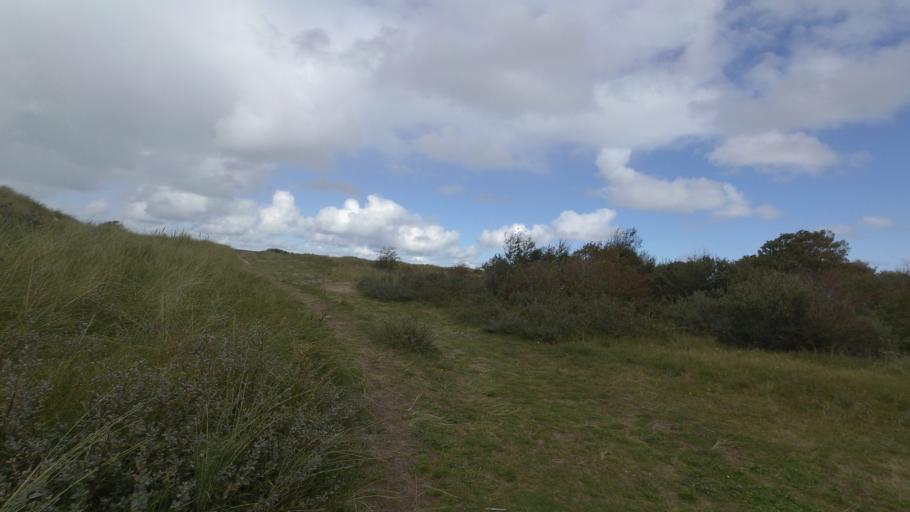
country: NL
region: Friesland
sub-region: Gemeente Ameland
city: Nes
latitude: 53.4516
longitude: 5.8378
